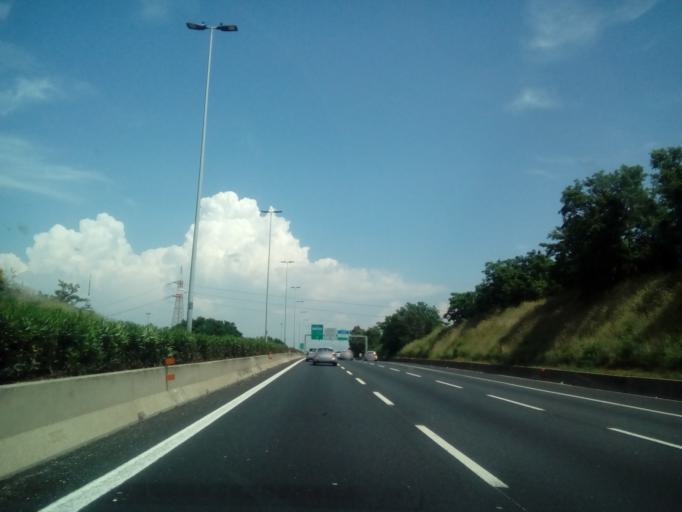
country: IT
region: Latium
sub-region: Citta metropolitana di Roma Capitale
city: Selcetta
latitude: 41.7986
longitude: 12.4724
